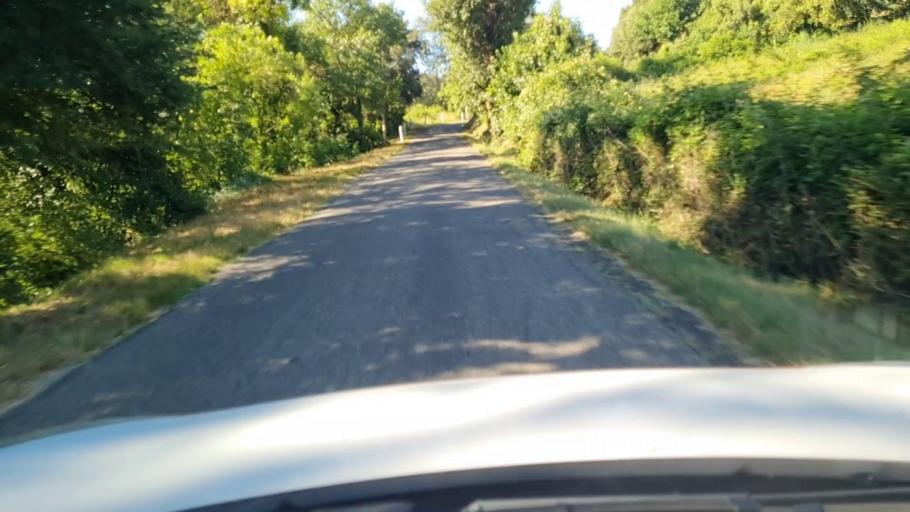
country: FR
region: Languedoc-Roussillon
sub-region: Departement du Gard
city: Sommieres
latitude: 43.8133
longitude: 4.0506
